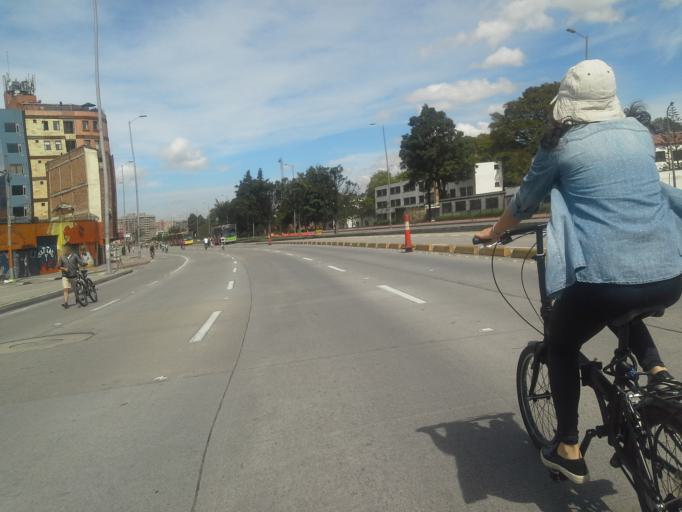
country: CO
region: Bogota D.C.
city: Bogota
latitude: 4.6323
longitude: -74.0849
